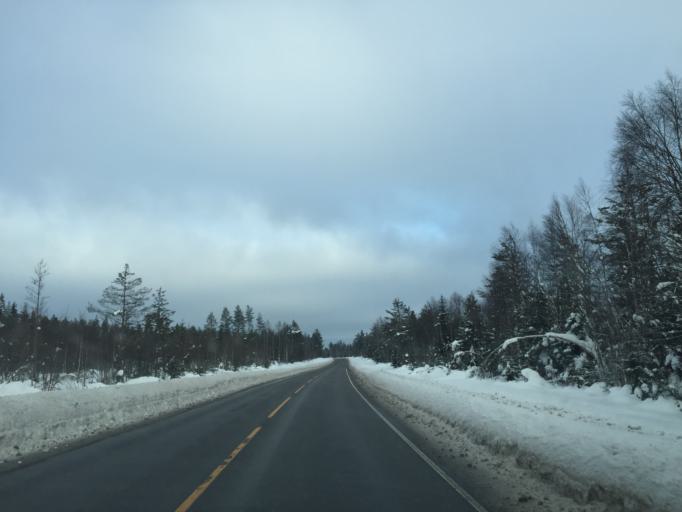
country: NO
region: Hedmark
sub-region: Trysil
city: Innbygda
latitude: 61.1398
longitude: 12.1170
